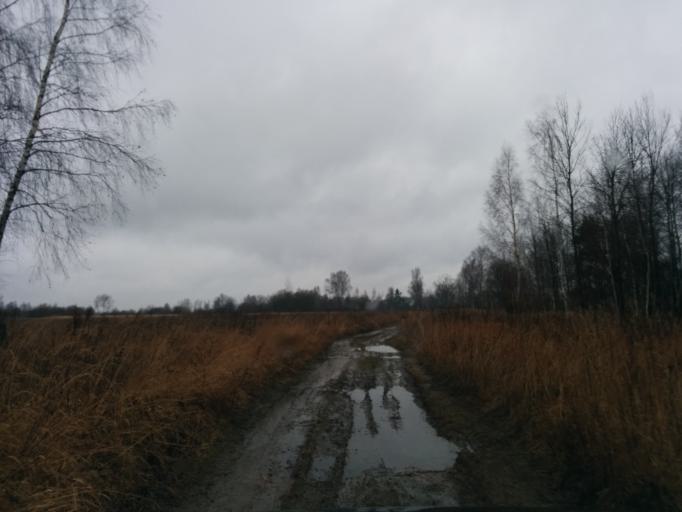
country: LV
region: Jelgava
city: Jelgava
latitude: 56.6781
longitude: 23.7088
